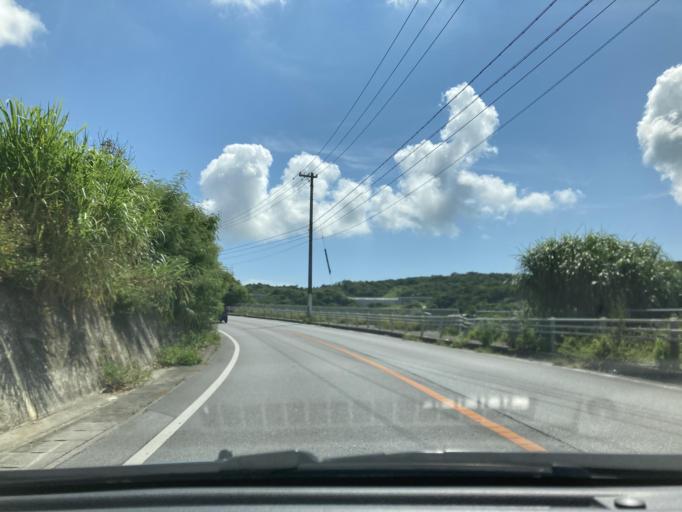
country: JP
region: Okinawa
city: Tomigusuku
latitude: 26.1616
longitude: 127.7634
